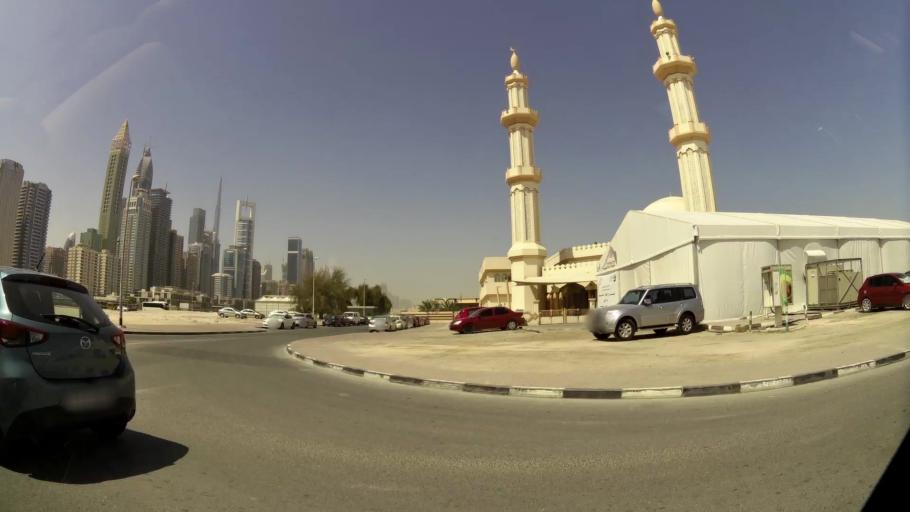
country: AE
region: Ash Shariqah
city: Sharjah
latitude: 25.2197
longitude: 55.2760
